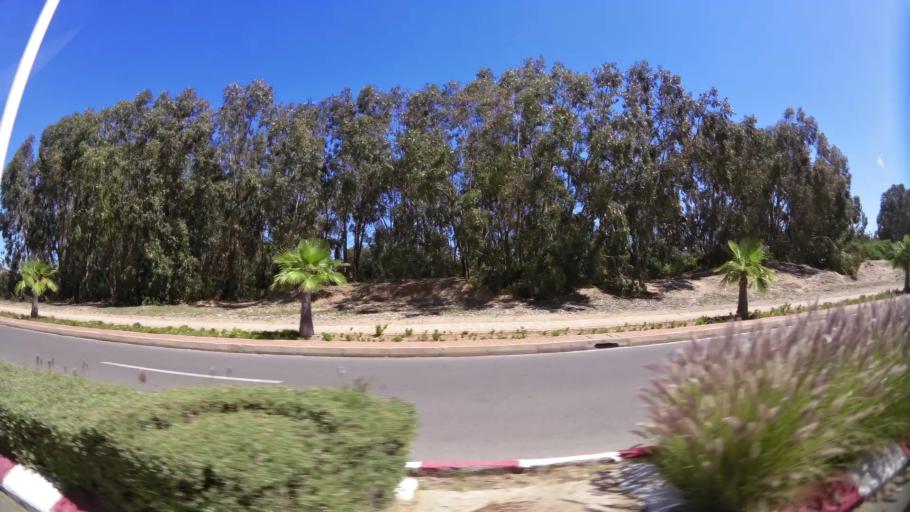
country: MA
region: Oriental
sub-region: Berkane-Taourirt
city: Madagh
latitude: 35.0945
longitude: -2.2688
